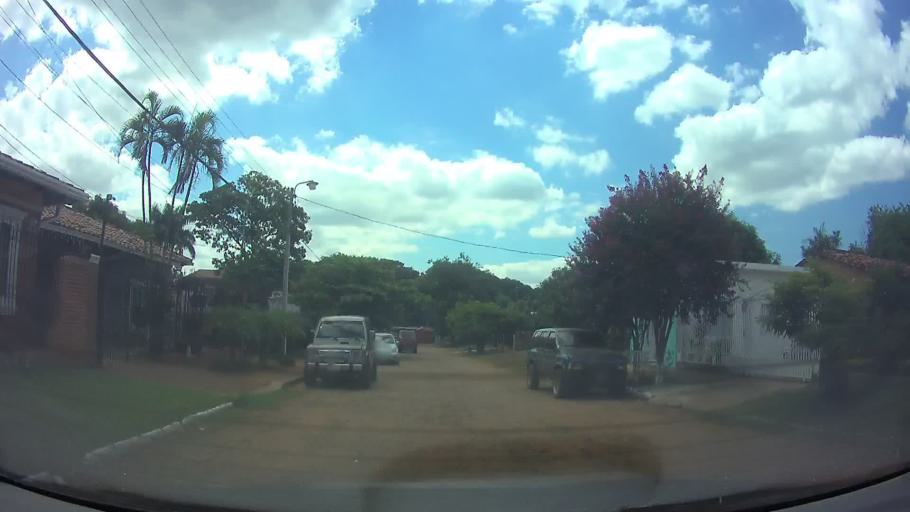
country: PY
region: Central
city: Itaugua
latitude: -25.3872
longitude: -57.3503
